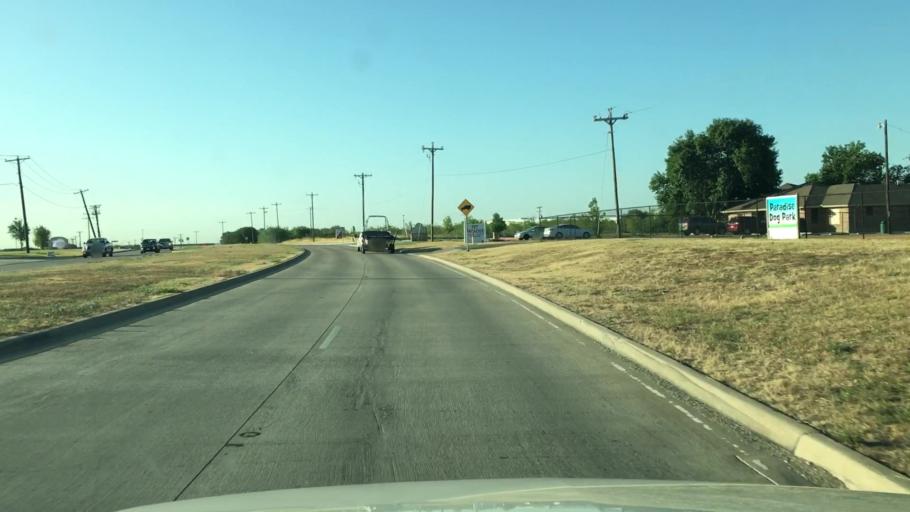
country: US
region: Texas
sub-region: Tarrant County
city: Crowley
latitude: 32.5433
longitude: -97.3654
